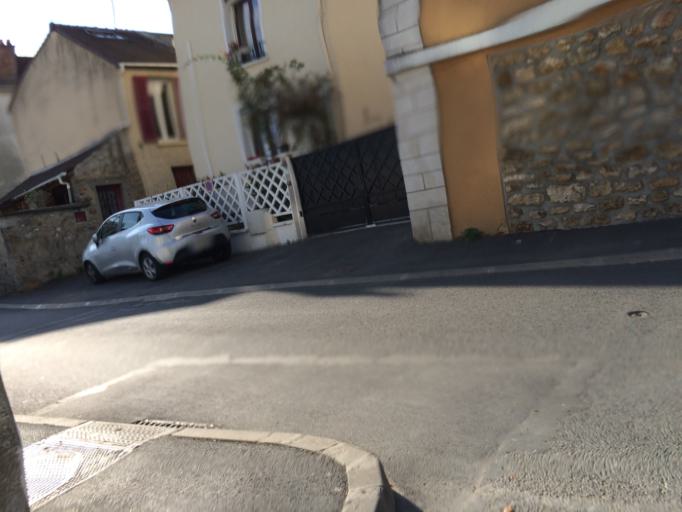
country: FR
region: Ile-de-France
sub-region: Departement de l'Essonne
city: Savigny-sur-Orge
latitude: 48.6721
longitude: 2.3492
